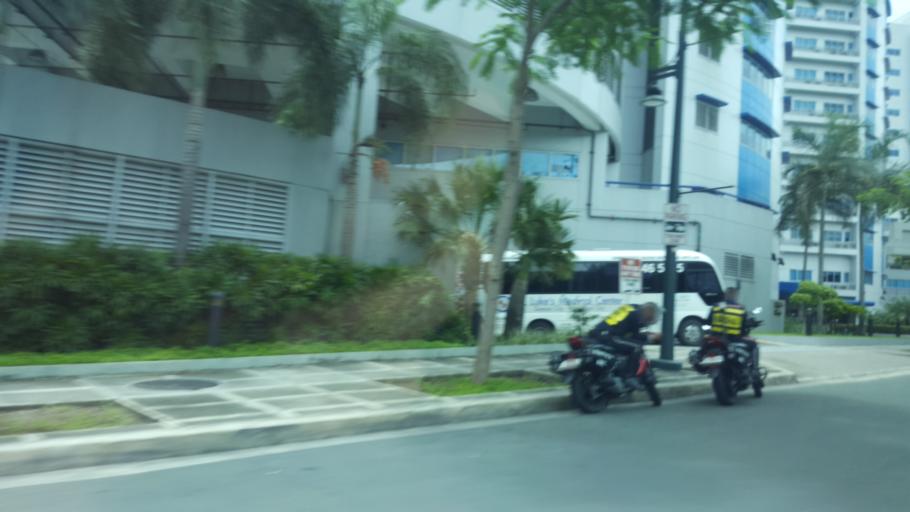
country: PH
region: Metro Manila
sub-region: Makati City
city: Makati City
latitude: 14.5560
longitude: 121.0491
